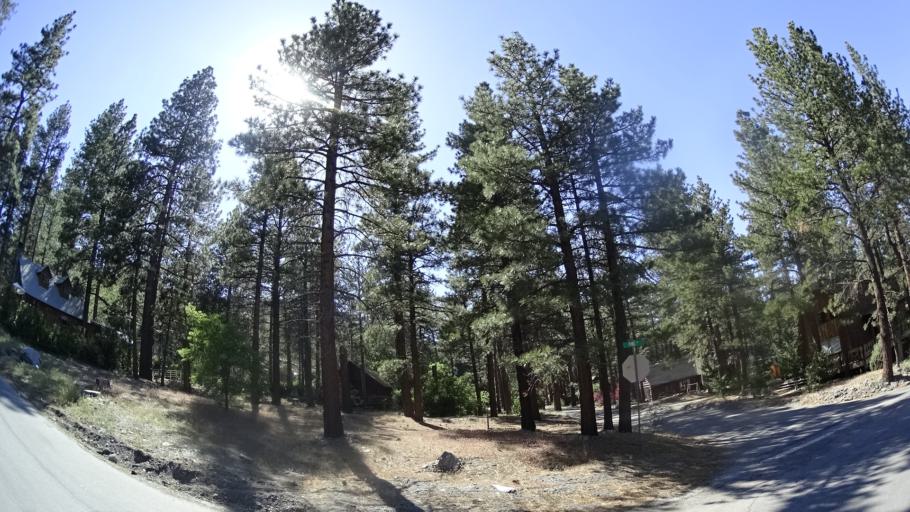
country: US
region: California
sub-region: San Bernardino County
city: Wrightwood
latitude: 34.3560
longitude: -117.6374
